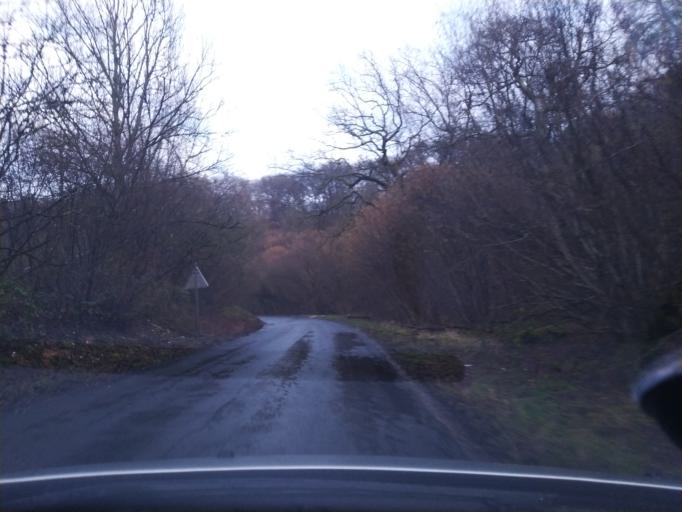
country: FR
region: Haute-Normandie
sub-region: Departement de la Seine-Maritime
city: Duclair
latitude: 49.4886
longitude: 0.9000
